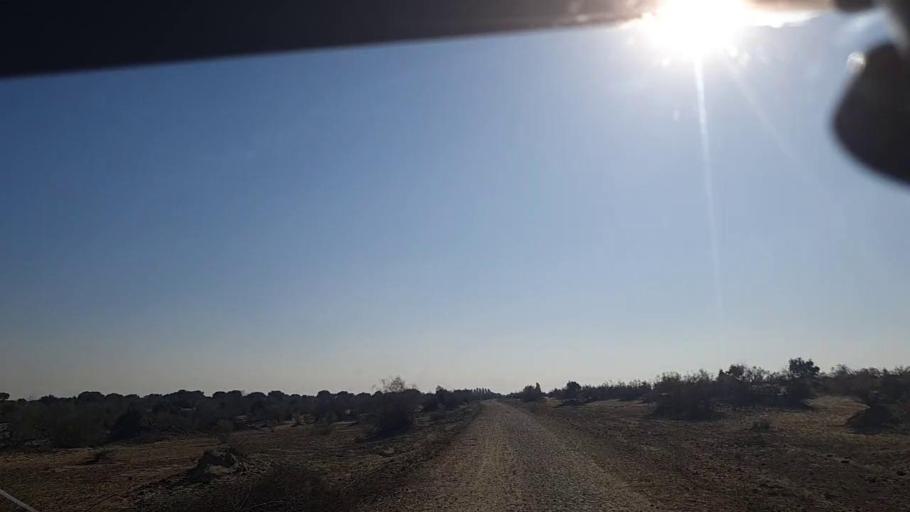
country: PK
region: Sindh
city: Khanpur
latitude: 27.6422
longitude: 69.4060
